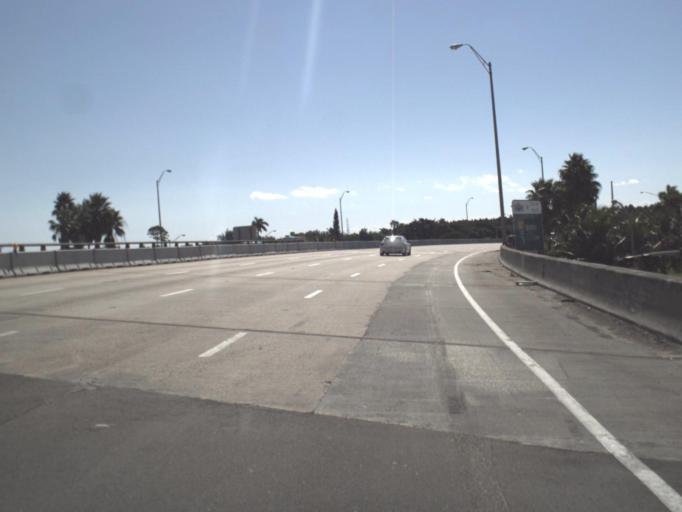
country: US
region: Florida
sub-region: Miami-Dade County
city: Richmond Heights
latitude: 25.6278
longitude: -80.3802
